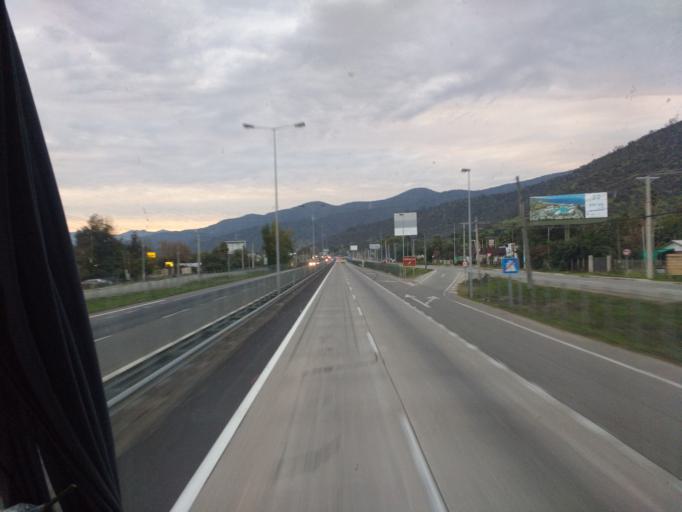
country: CL
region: Santiago Metropolitan
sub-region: Provincia de Chacabuco
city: Lampa
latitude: -33.4193
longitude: -71.0475
